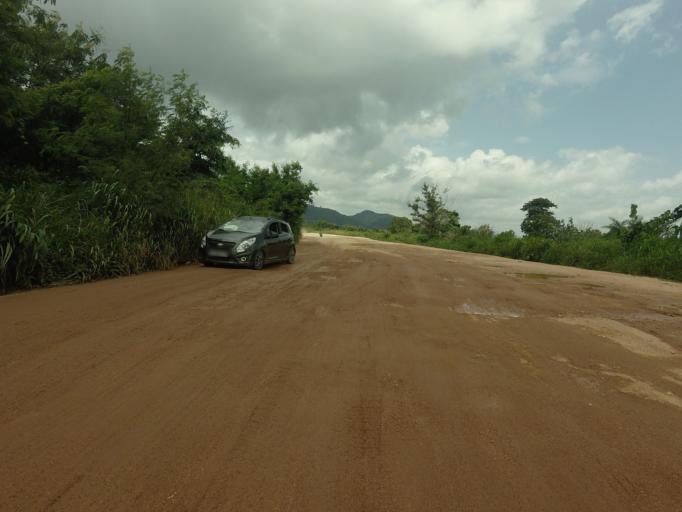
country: GH
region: Volta
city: Ho
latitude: 6.7010
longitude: 0.3352
